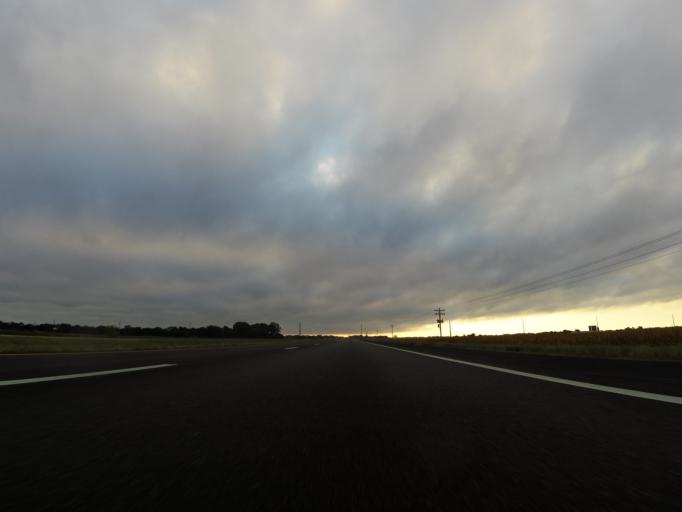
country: US
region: Kansas
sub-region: Sedgwick County
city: Colwich
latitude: 37.8248
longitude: -97.5327
